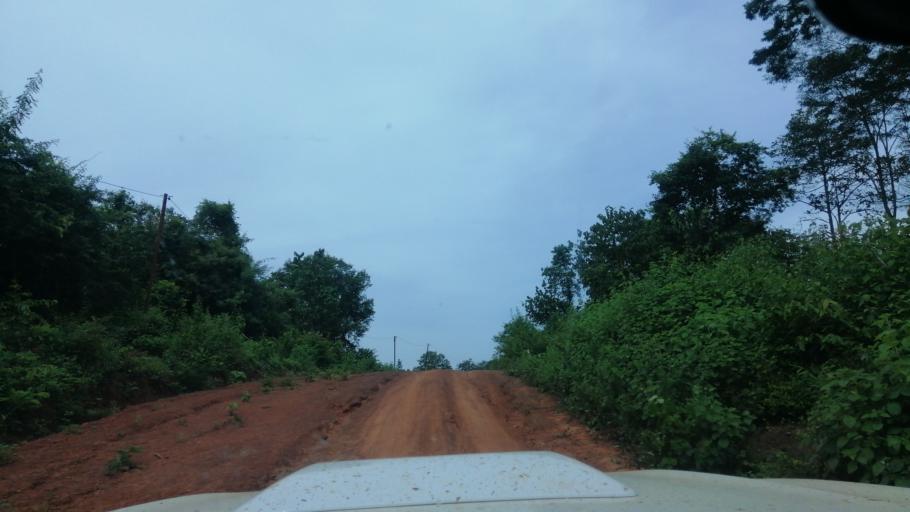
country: TH
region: Loei
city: Na Haeo
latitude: 17.5782
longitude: 101.1585
